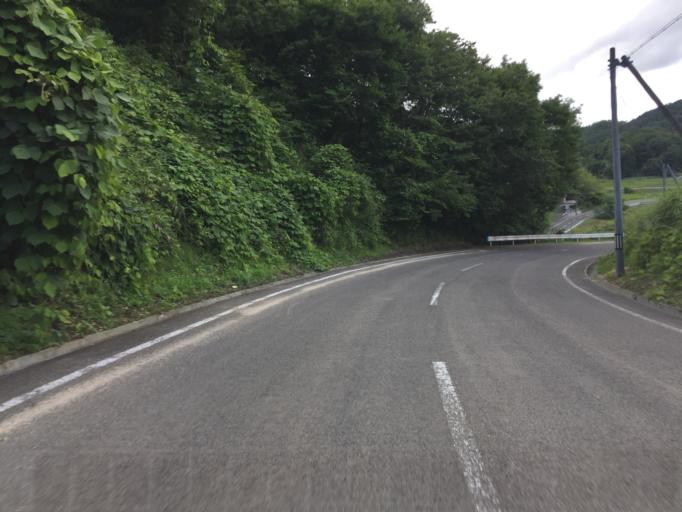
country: JP
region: Fukushima
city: Fukushima-shi
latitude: 37.6825
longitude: 140.5234
